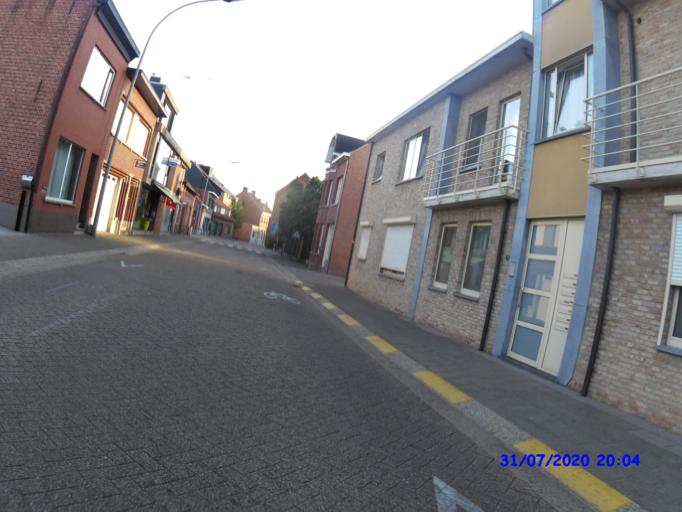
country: BE
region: Flanders
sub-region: Provincie Antwerpen
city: Vosselaar
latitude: 51.2425
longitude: 4.8996
